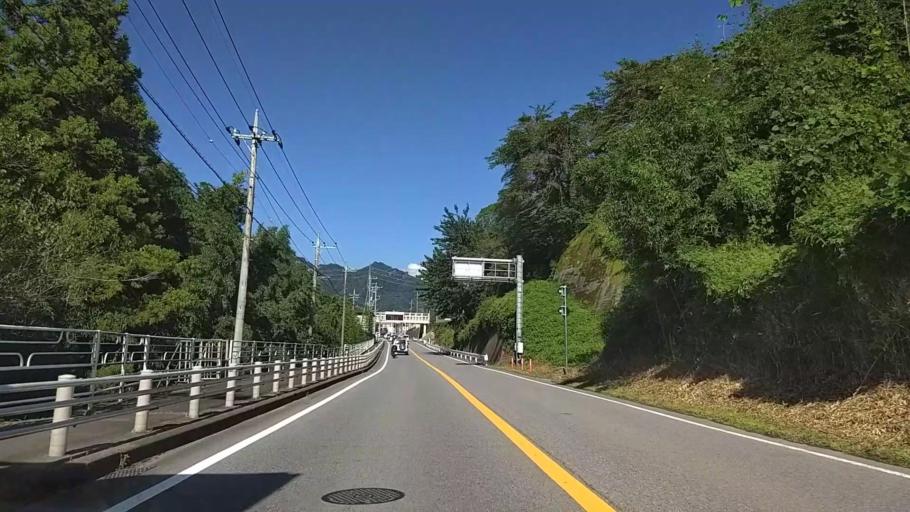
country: JP
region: Gunma
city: Annaka
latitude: 36.3342
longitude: 138.7435
